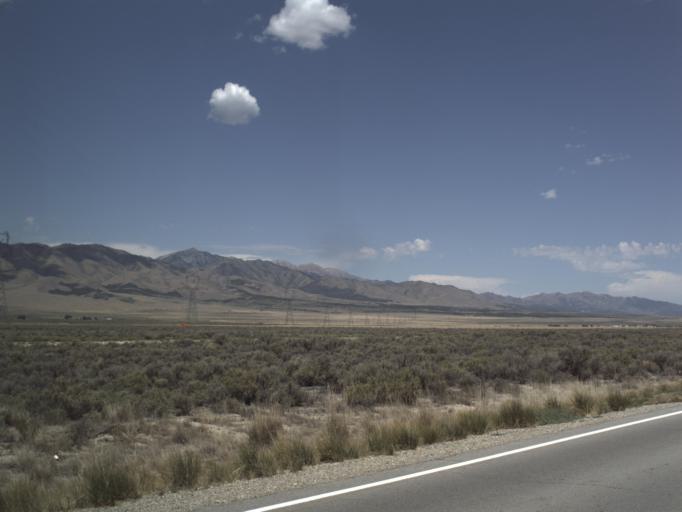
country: US
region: Utah
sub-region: Tooele County
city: Tooele
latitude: 40.3461
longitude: -112.4113
